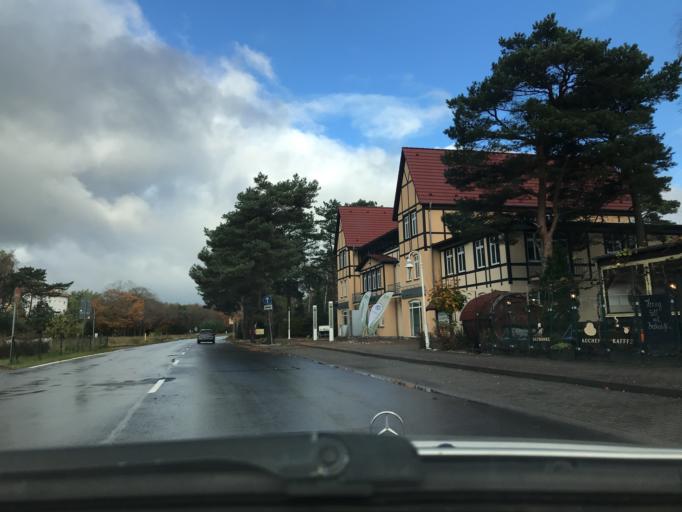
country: DE
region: Mecklenburg-Vorpommern
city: Karlshagen
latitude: 54.1177
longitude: 13.8307
